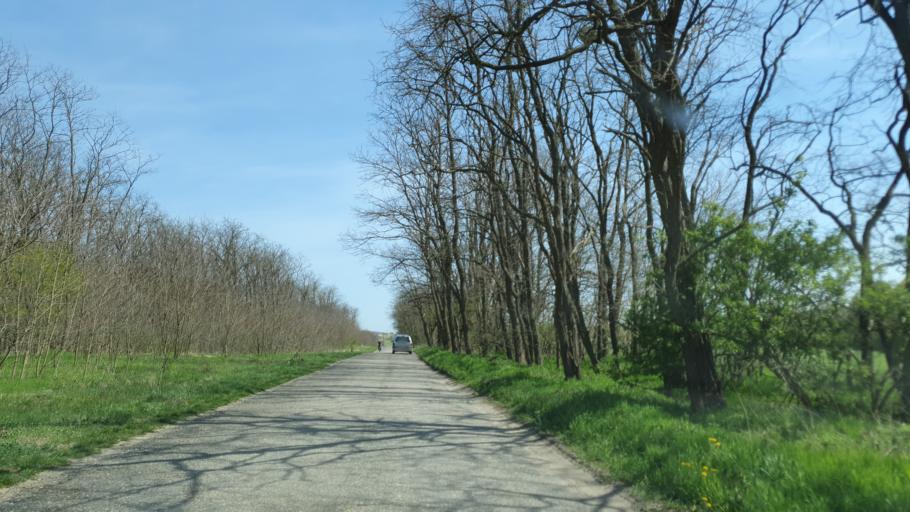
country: HU
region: Komarom-Esztergom
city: Oroszlany
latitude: 47.4961
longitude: 18.2899
